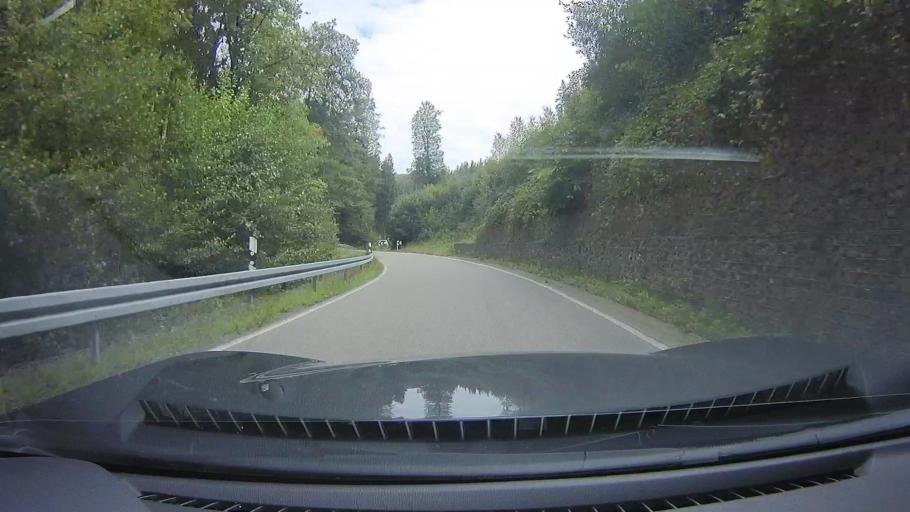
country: DE
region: Baden-Wuerttemberg
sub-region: Regierungsbezirk Stuttgart
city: Wustenrot
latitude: 49.0606
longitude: 9.4598
